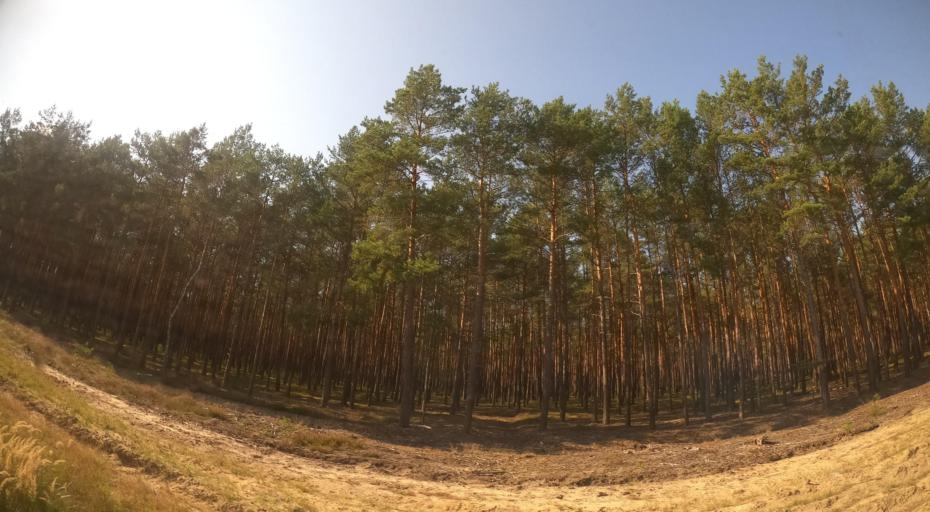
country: PL
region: Lubusz
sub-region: Powiat zielonogorski
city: Nowogrod Bobrzanski
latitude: 51.8260
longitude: 15.2538
